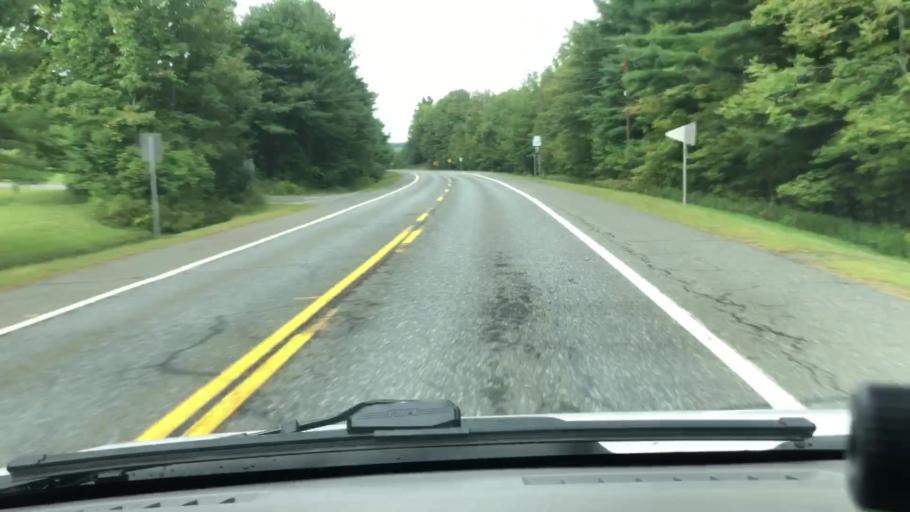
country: US
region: Massachusetts
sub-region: Franklin County
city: Ashfield
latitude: 42.4577
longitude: -72.8052
